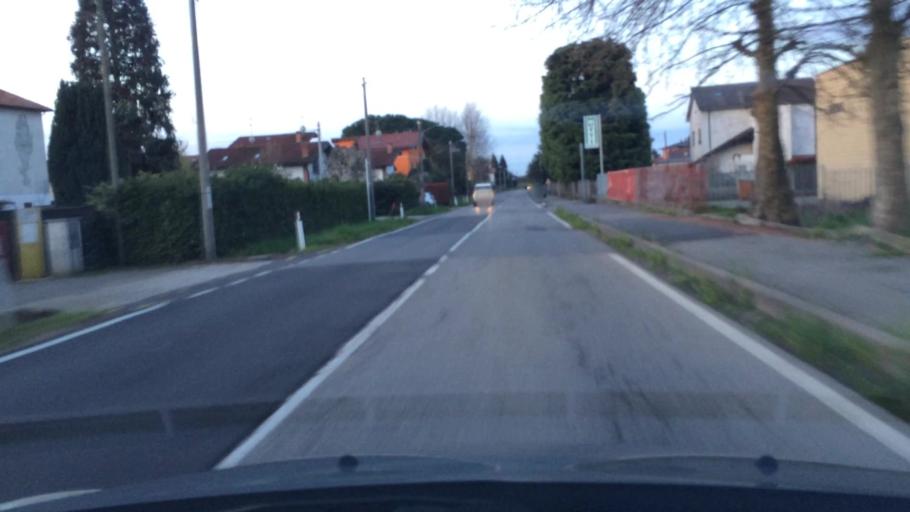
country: IT
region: Lombardy
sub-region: Provincia di Como
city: Bregnano
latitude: 45.7046
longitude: 9.0626
